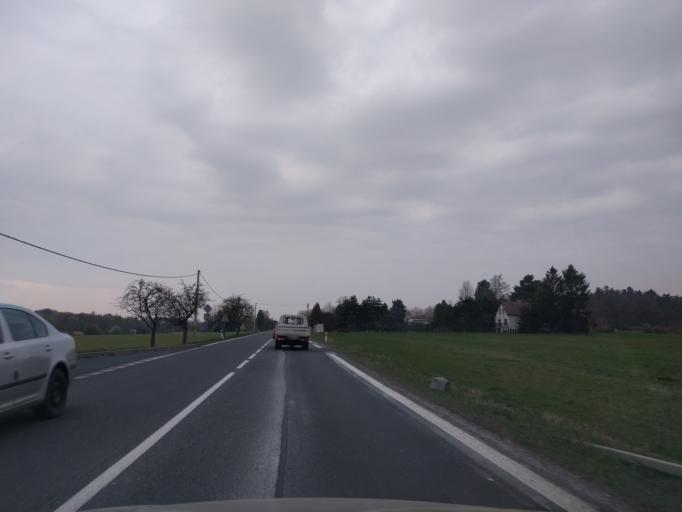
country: CZ
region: Central Bohemia
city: Mukarov
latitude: 49.9884
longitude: 14.7670
